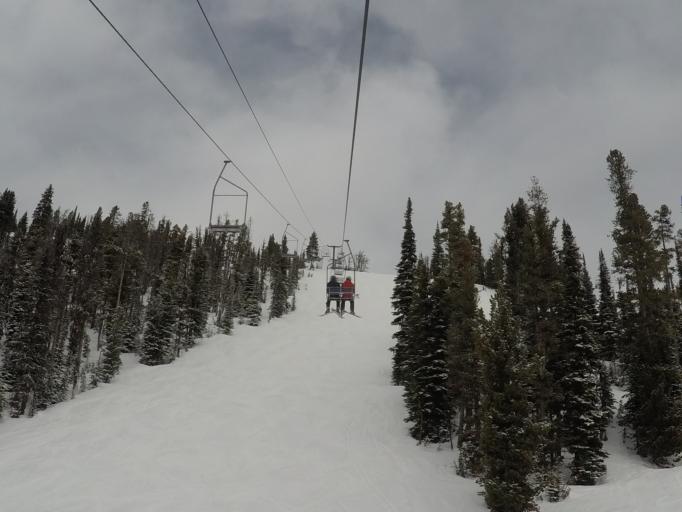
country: US
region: Montana
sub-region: Meagher County
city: White Sulphur Springs
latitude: 46.8363
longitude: -110.7139
